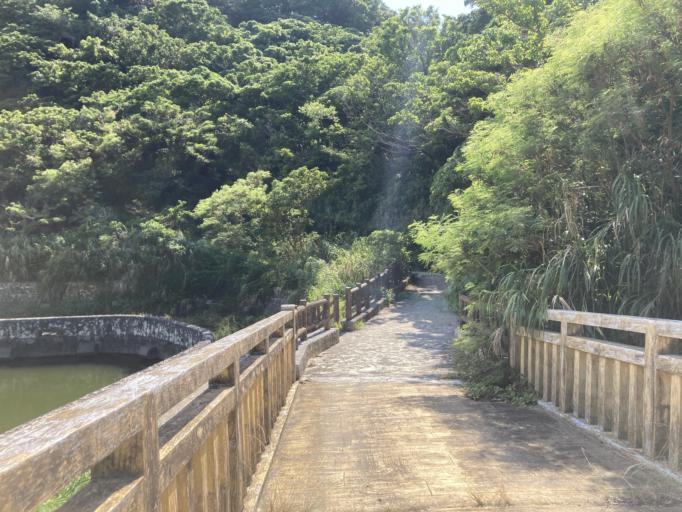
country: JP
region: Okinawa
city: Naha-shi
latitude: 26.2098
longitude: 127.7193
